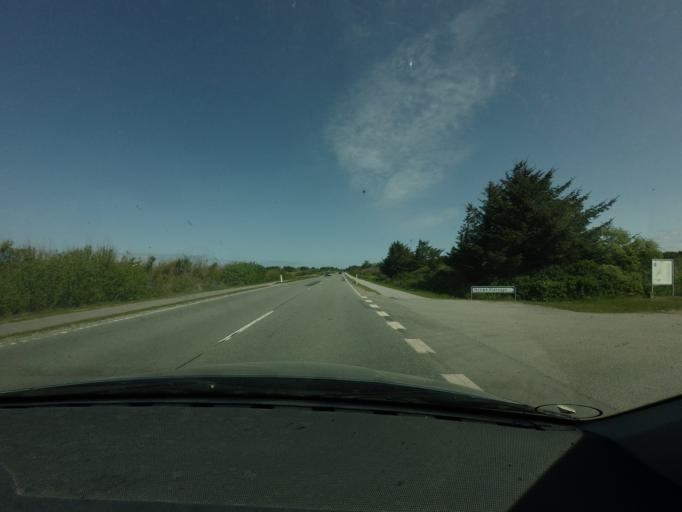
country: DK
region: North Denmark
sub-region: Jammerbugt Kommune
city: Pandrup
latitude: 57.3533
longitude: 9.7071
